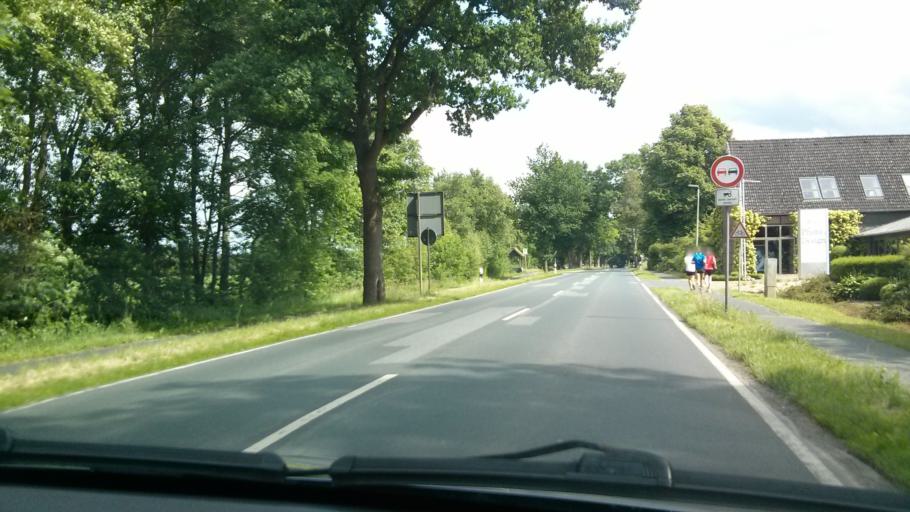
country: DE
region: Lower Saxony
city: Schiffdorf
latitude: 53.5236
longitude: 8.6663
